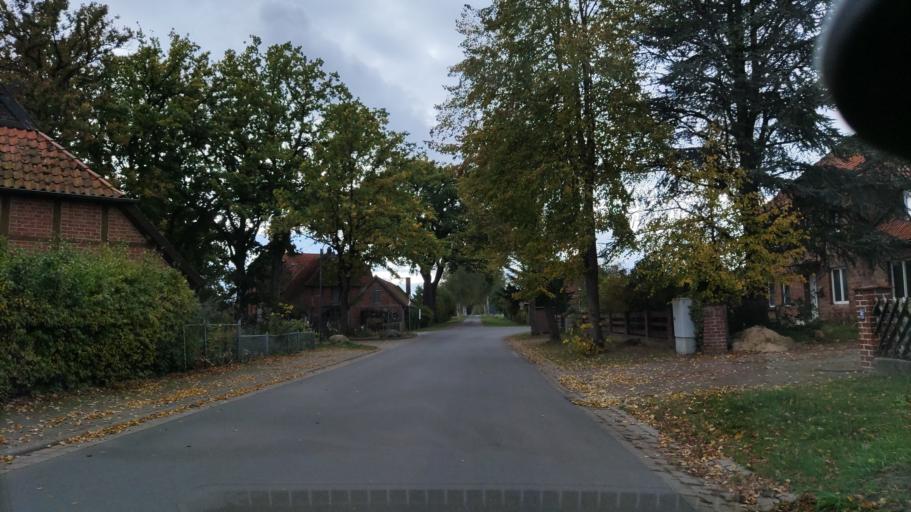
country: DE
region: Lower Saxony
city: Jelmstorf
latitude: 53.1450
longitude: 10.5330
